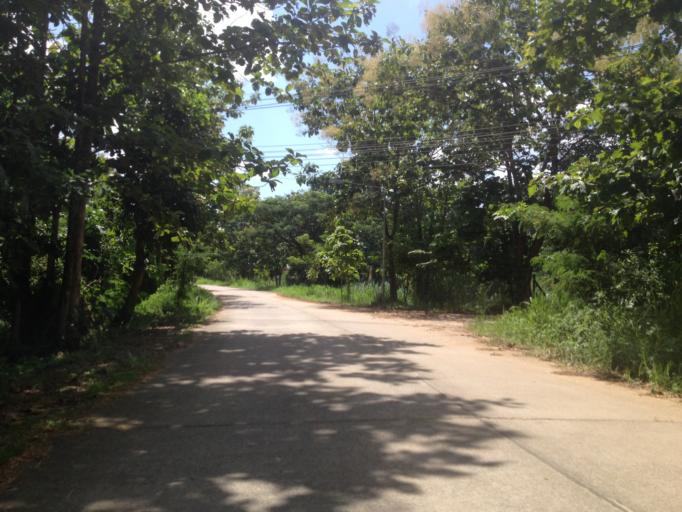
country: TH
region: Chiang Mai
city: Chiang Mai
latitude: 18.7667
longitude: 98.9300
